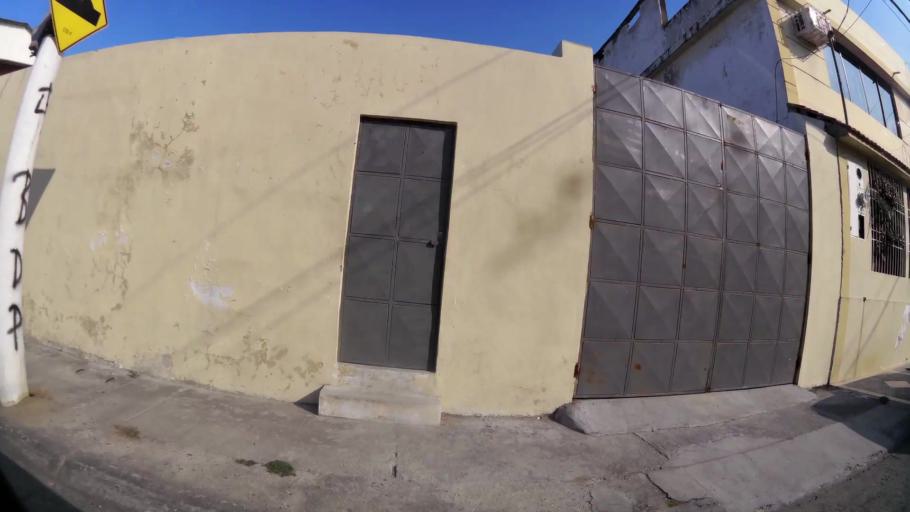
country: EC
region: Guayas
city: Guayaquil
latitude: -2.1508
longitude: -79.9085
